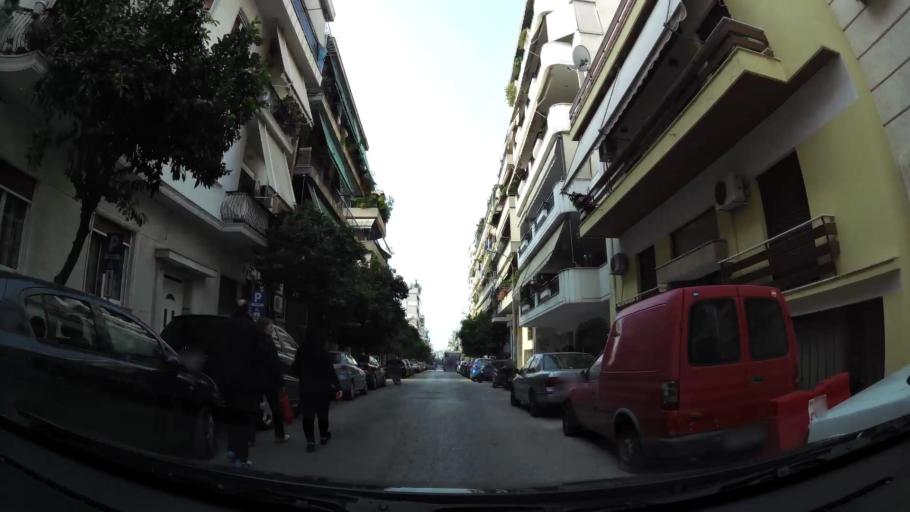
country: GR
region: Attica
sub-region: Nomarchia Athinas
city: Kallithea
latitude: 37.9581
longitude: 23.6974
